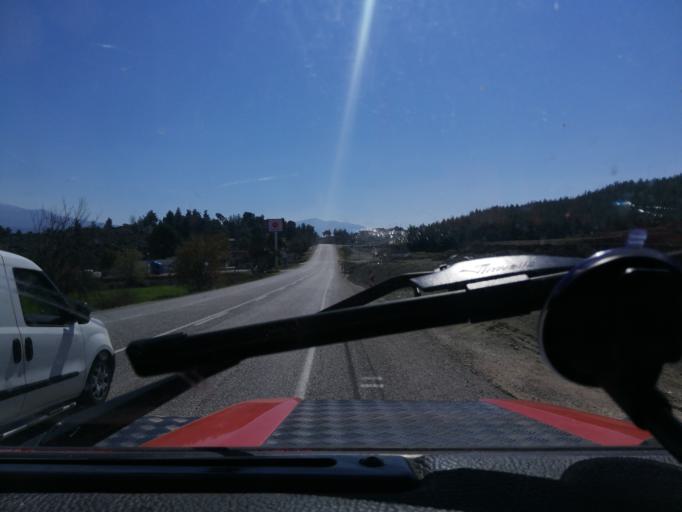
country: TR
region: Mugla
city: Kemer
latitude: 36.6147
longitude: 29.3575
